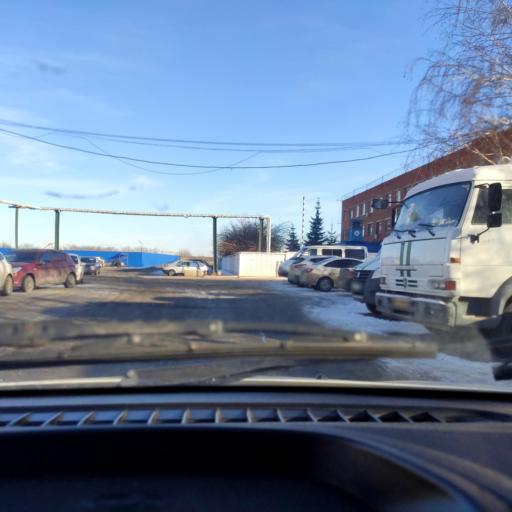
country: RU
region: Samara
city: Tol'yatti
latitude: 53.5745
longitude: 49.3452
